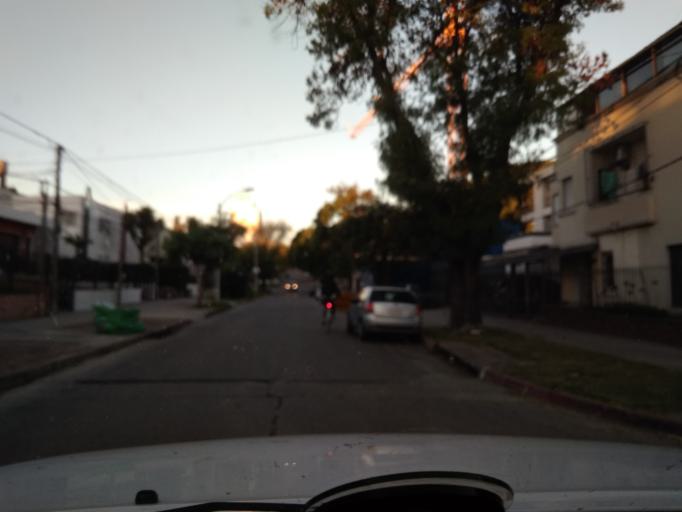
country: UY
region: Montevideo
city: Montevideo
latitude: -34.8938
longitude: -56.1197
